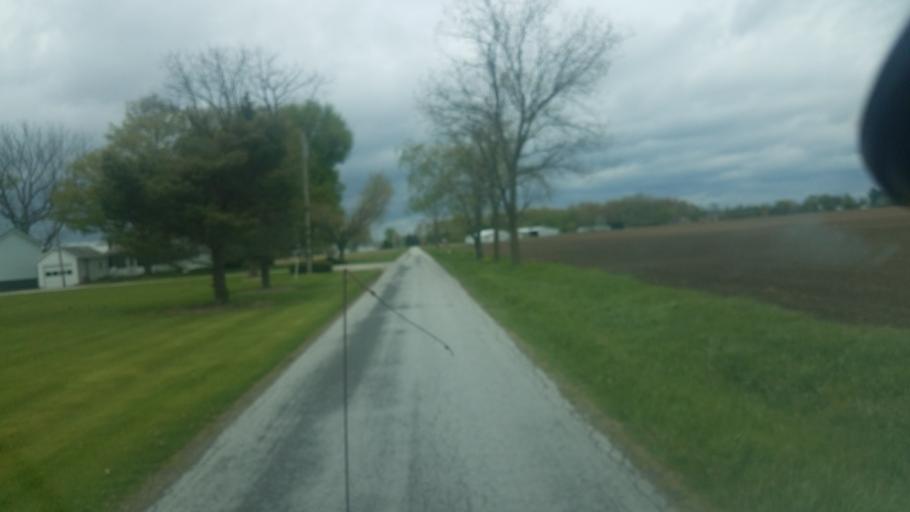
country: US
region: Ohio
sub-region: Marion County
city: Prospect
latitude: 40.5140
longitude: -83.2387
